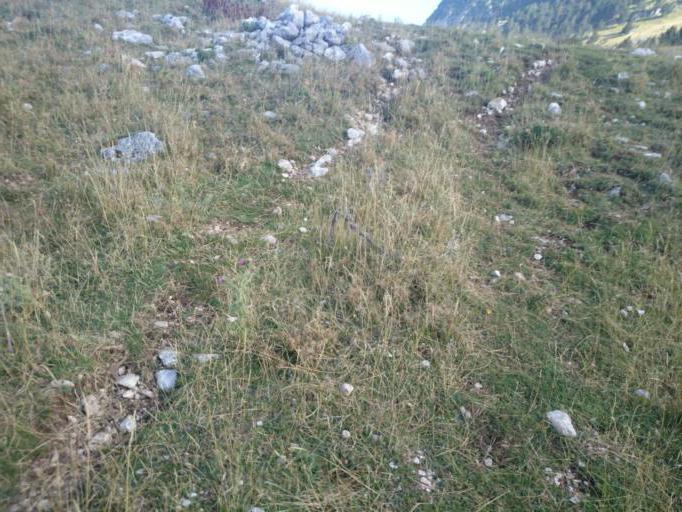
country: AL
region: Elbasan
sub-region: Rrethi i Gramshit
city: Kushove
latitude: 40.7313
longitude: 20.1491
